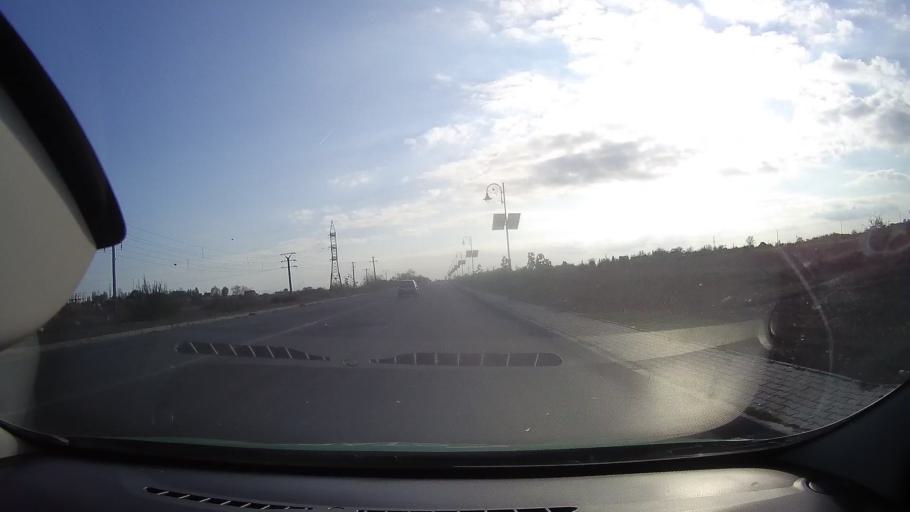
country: RO
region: Constanta
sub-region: Comuna Navodari
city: Navodari
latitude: 44.3037
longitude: 28.6147
